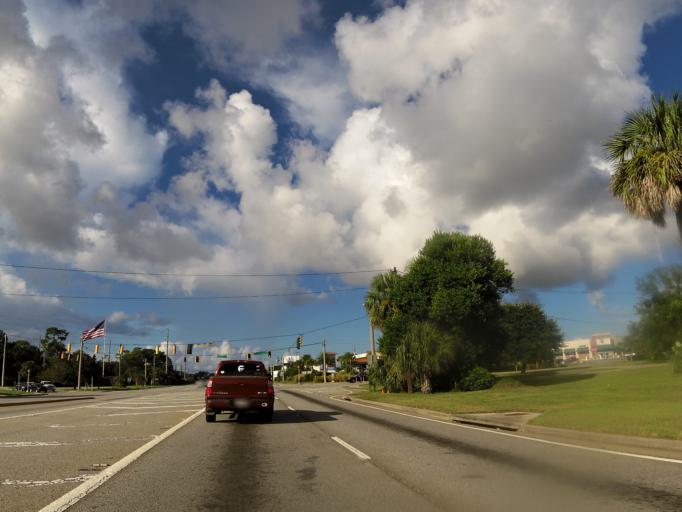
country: US
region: Georgia
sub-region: Glynn County
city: Brunswick
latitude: 31.1612
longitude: -81.4769
